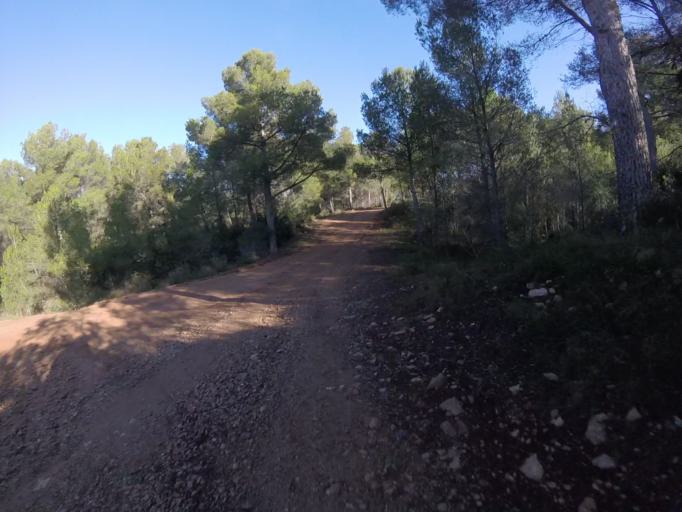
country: ES
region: Valencia
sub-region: Provincia de Castello
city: Alcala de Xivert
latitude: 40.2975
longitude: 0.2689
